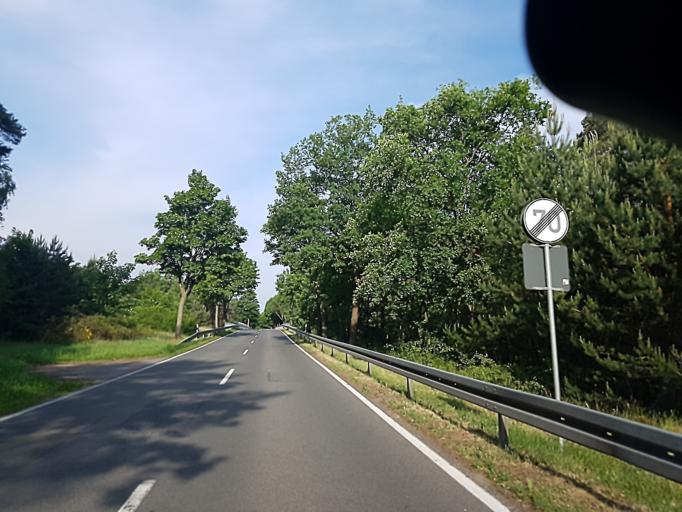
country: DE
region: Brandenburg
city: Niemegk
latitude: 52.0554
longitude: 12.6508
